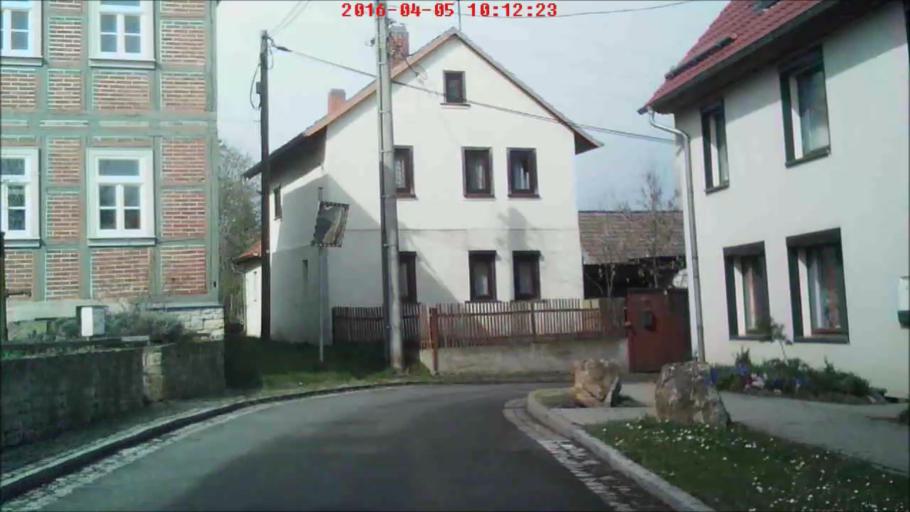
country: DE
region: Thuringia
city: Witterda
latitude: 51.0245
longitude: 10.9134
